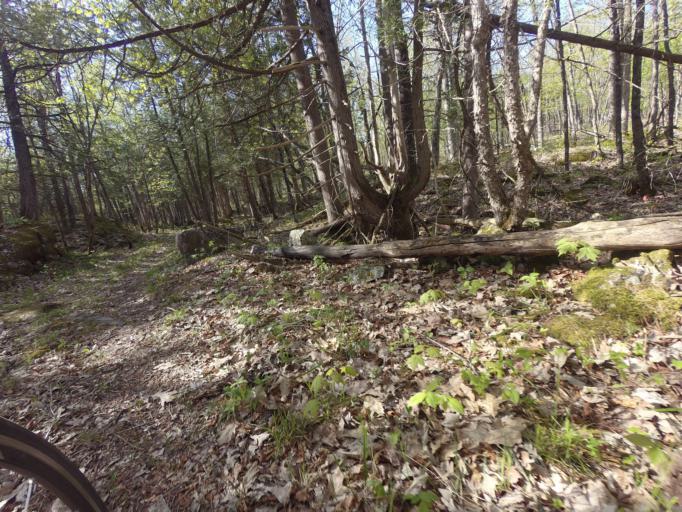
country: CA
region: Ontario
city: Arnprior
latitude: 45.4707
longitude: -76.3006
